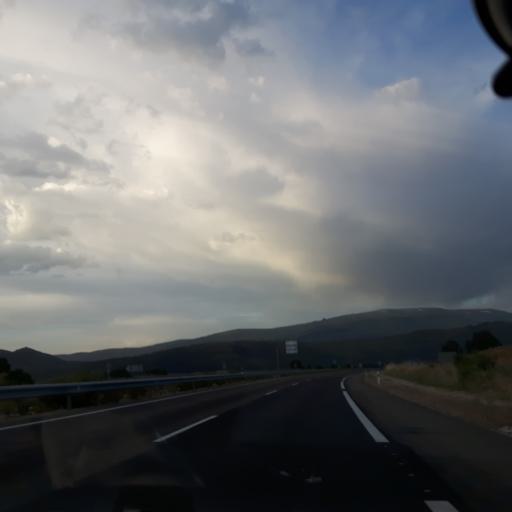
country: ES
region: Castille and Leon
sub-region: Provincia de Salamanca
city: Nava de Bejar
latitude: 40.4635
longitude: -5.6778
